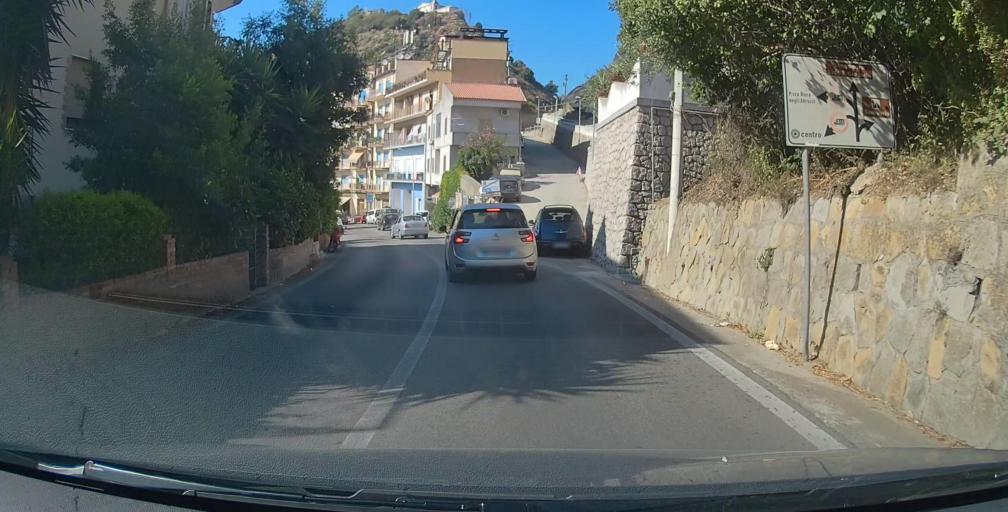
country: IT
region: Sicily
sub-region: Messina
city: Capo d'Orlando
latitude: 38.1614
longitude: 14.7488
